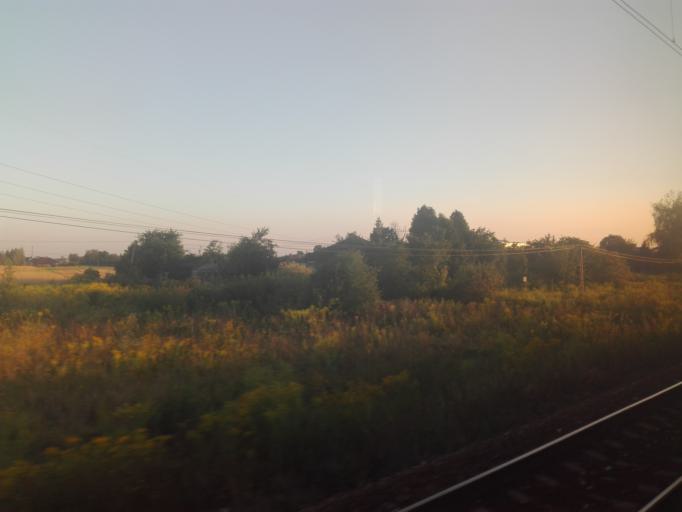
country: PL
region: Masovian Voivodeship
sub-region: Powiat warszawski zachodni
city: Bieniewice
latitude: 52.1862
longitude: 20.5794
